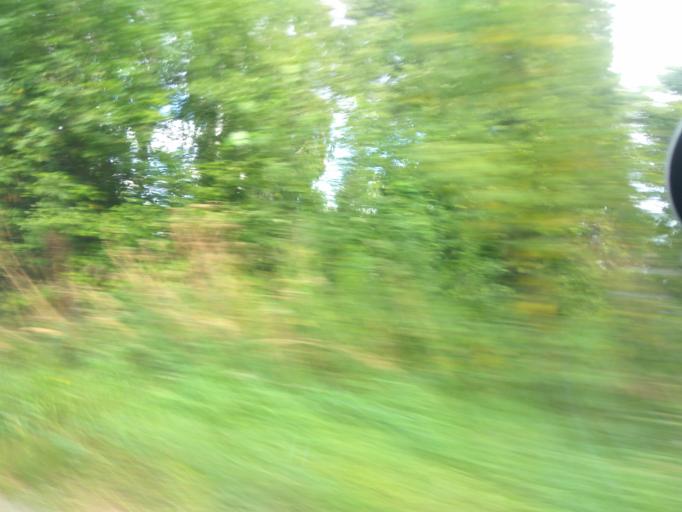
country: RU
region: Moskovskaya
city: Bronnitsy
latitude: 55.4849
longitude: 38.2369
